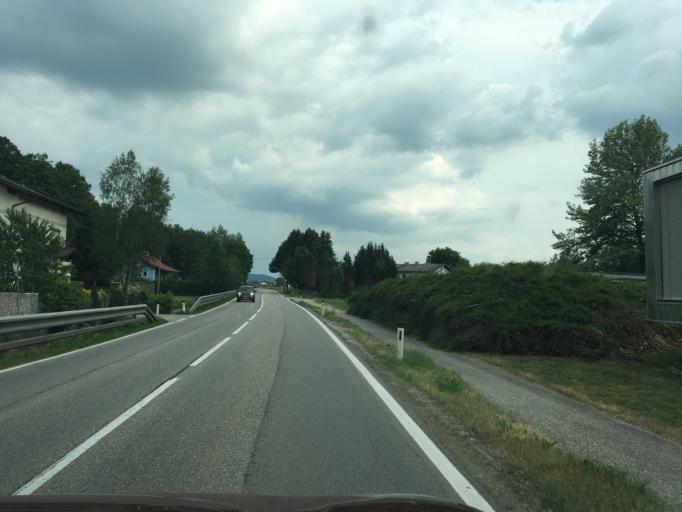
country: AT
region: Upper Austria
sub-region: Politischer Bezirk Braunau am Inn
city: Altheim
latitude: 48.1397
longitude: 13.1369
